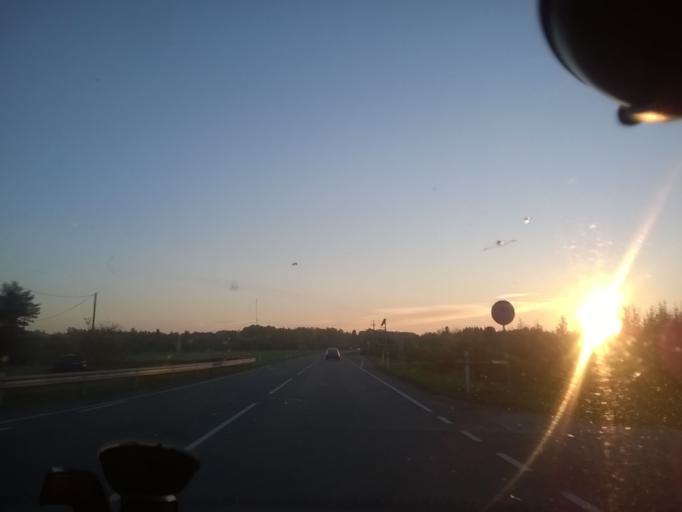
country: EE
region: Laeaene
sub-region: Ridala Parish
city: Uuemoisa
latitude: 58.9626
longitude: 23.8238
